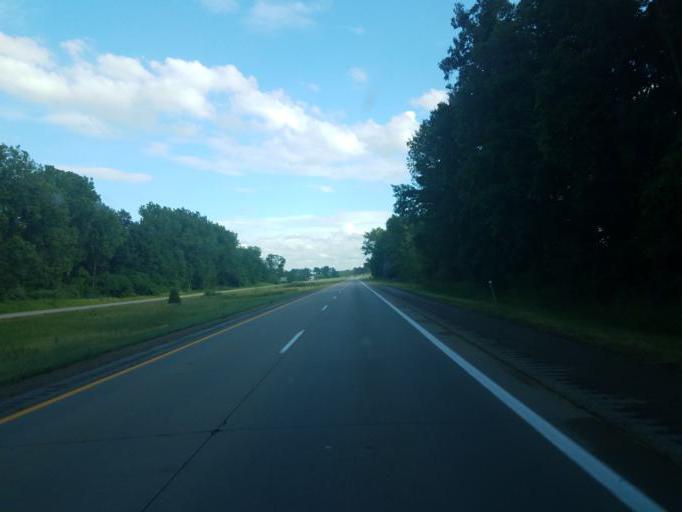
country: US
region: Indiana
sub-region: Steuben County
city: Fremont
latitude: 41.7769
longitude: -84.9896
